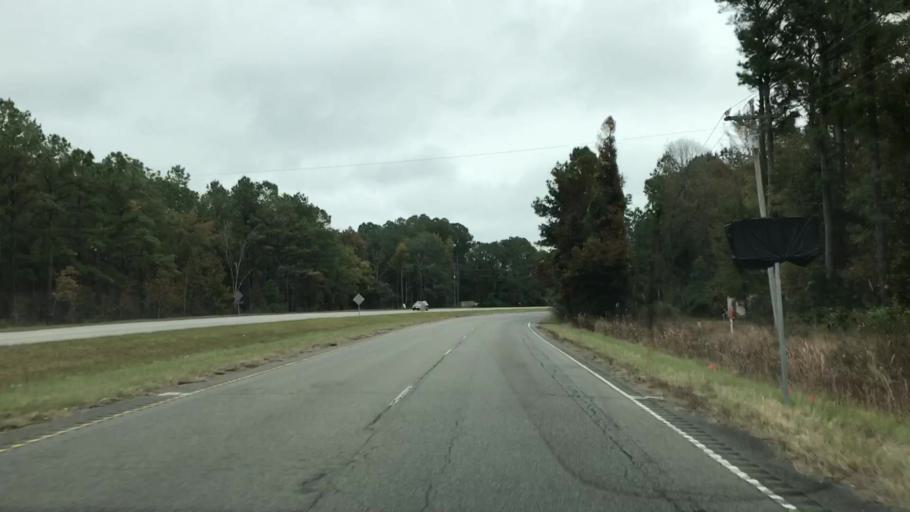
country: US
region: South Carolina
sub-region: Charleston County
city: Awendaw
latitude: 33.0360
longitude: -79.6184
